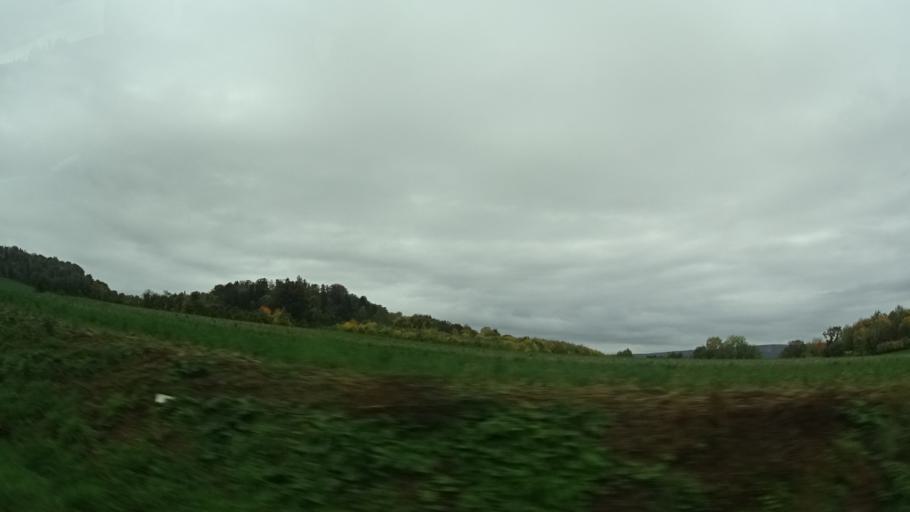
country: DE
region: Thuringia
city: Wernburg
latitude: 50.6822
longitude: 11.5965
